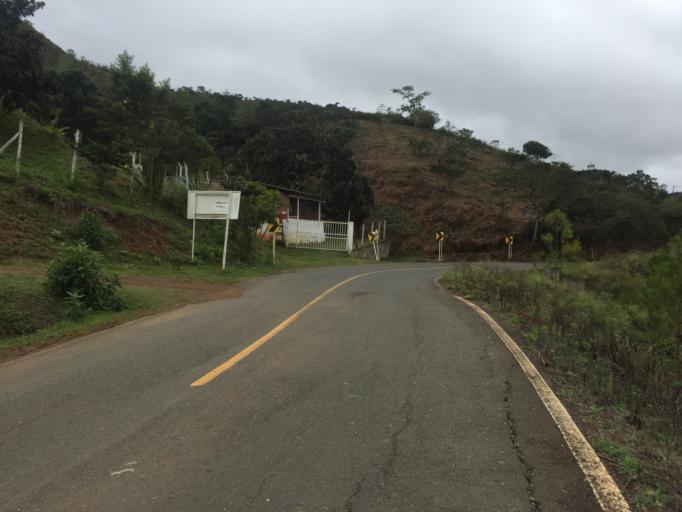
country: CO
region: Valle del Cauca
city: Dagua
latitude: 3.6985
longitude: -76.5879
